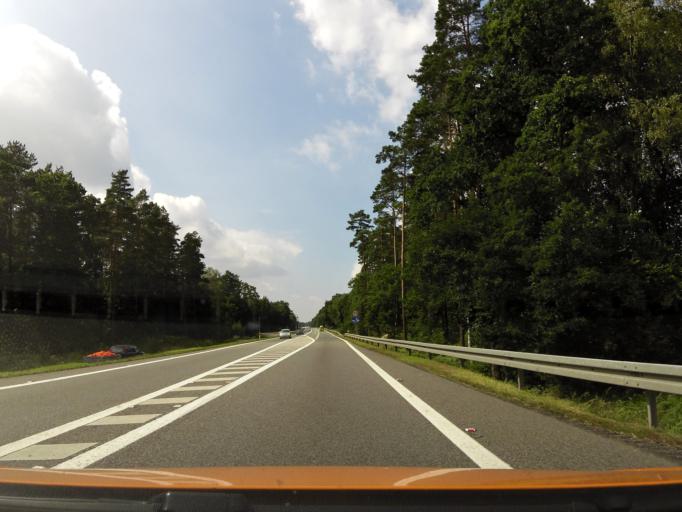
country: PL
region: West Pomeranian Voivodeship
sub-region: Powiat goleniowski
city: Osina
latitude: 53.6324
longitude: 14.9995
